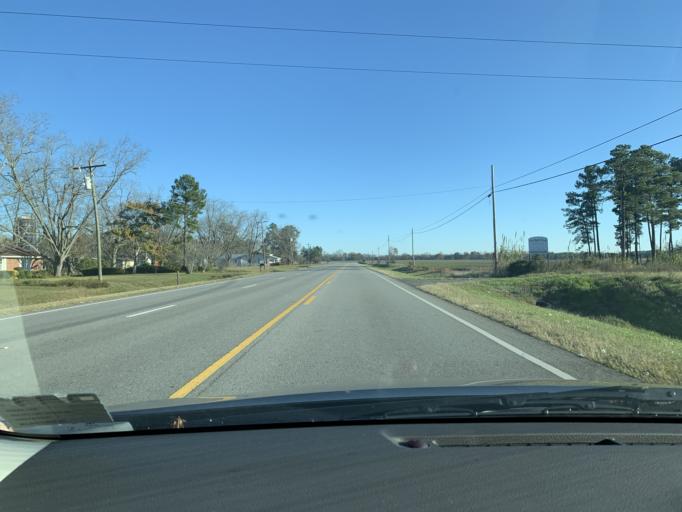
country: US
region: Georgia
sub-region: Ben Hill County
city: Fitzgerald
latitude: 31.6616
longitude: -83.2386
